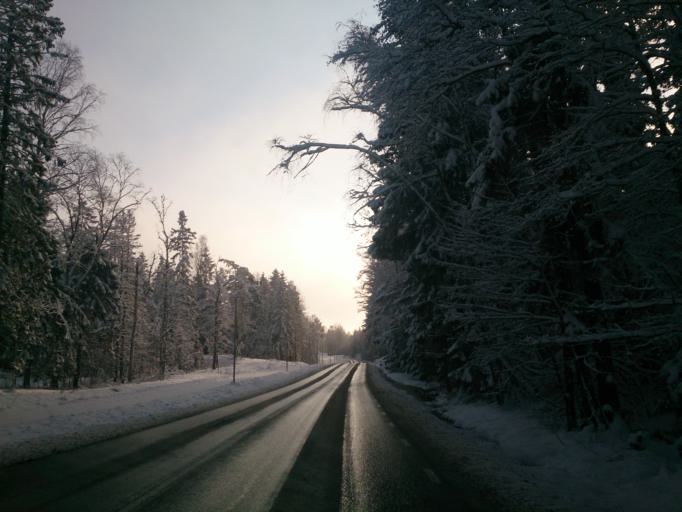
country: SE
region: Stockholm
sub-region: Varmdo Kommun
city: Hemmesta
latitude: 59.2944
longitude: 18.5182
